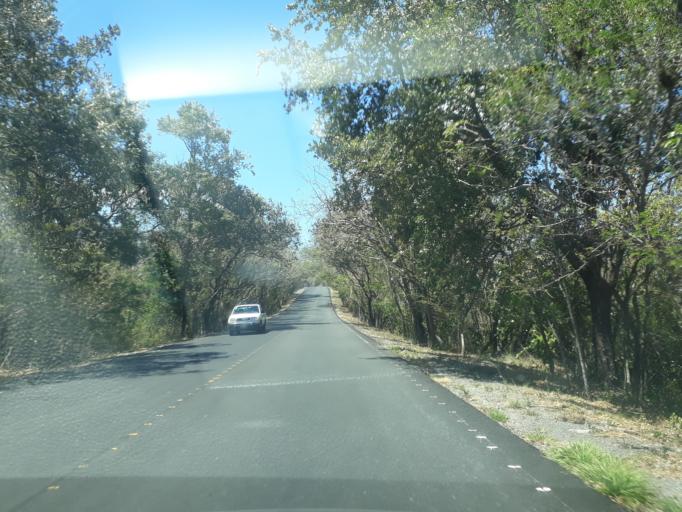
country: CR
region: Guanacaste
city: La Cruz
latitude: 10.8767
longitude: -85.5825
